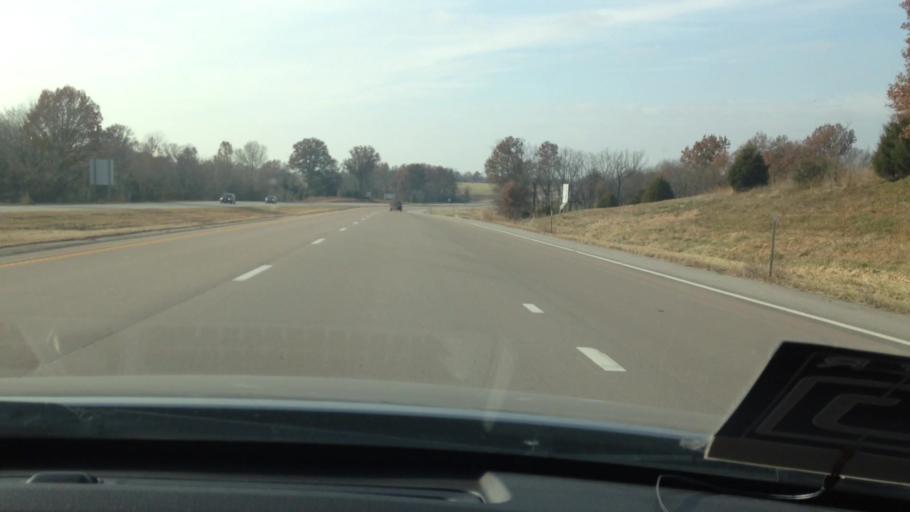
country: US
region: Missouri
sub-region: Cass County
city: Garden City
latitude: 38.4684
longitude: -94.0076
